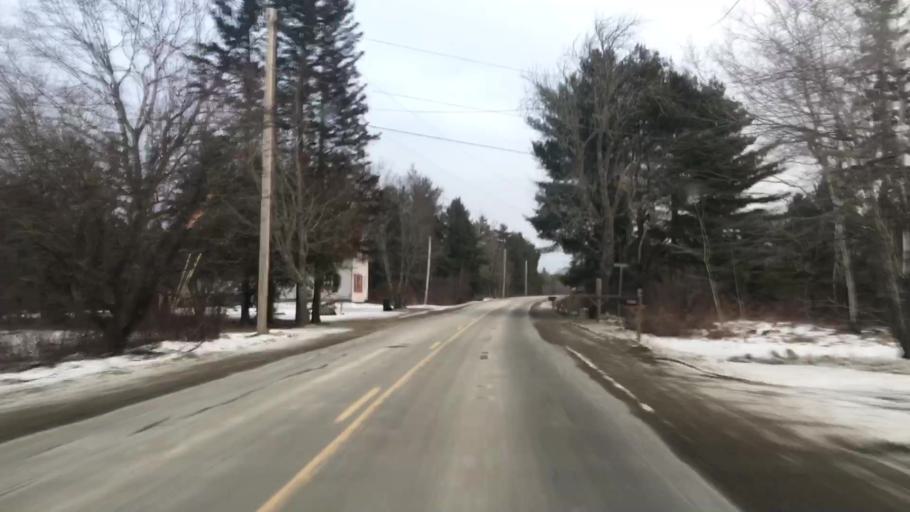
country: US
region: Maine
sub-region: Hancock County
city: Franklin
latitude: 44.6893
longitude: -68.3489
